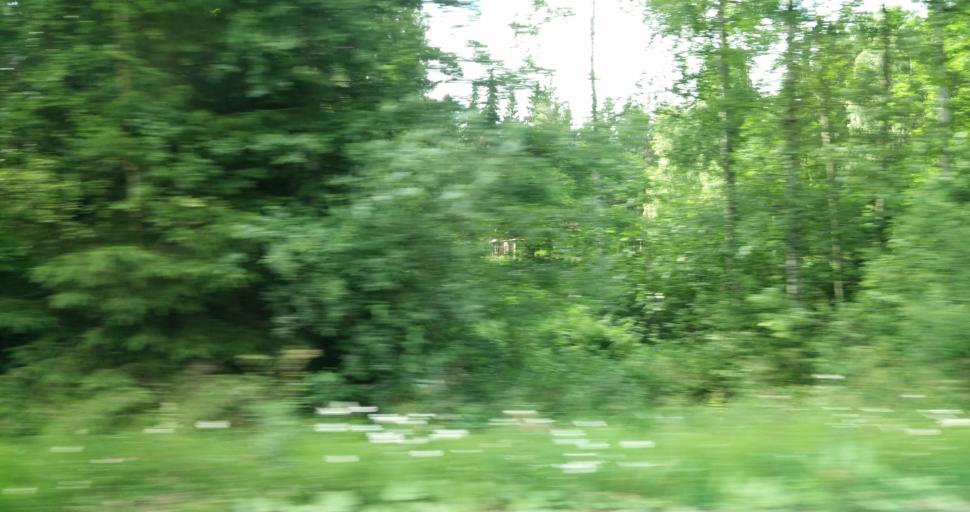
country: SE
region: Vaermland
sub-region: Hagfors Kommun
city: Ekshaerad
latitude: 60.0178
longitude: 13.4768
